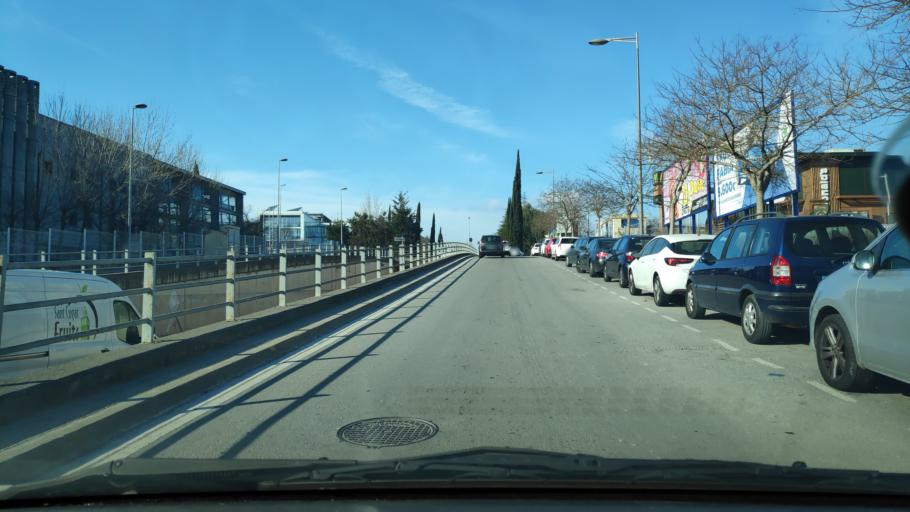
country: ES
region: Catalonia
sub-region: Provincia de Barcelona
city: Sant Cugat del Valles
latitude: 41.4764
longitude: 2.0975
